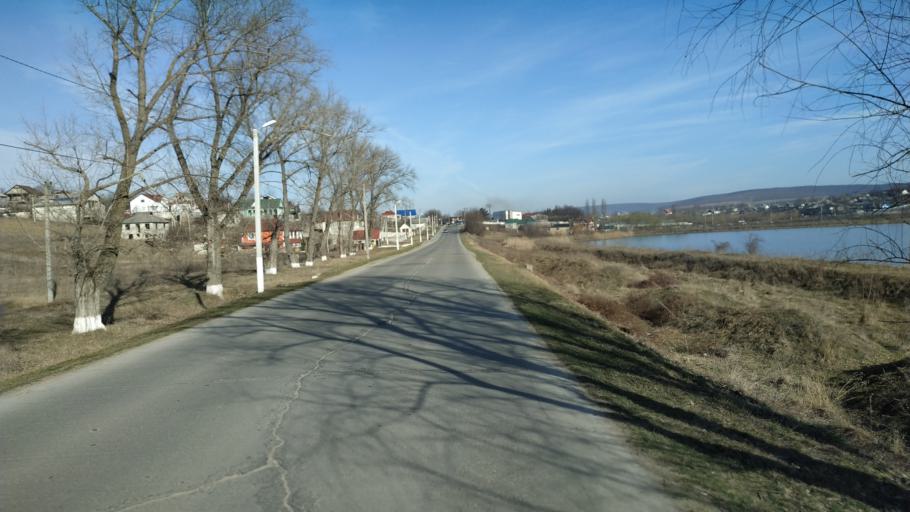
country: MD
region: Chisinau
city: Vatra
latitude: 47.0002
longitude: 28.6732
